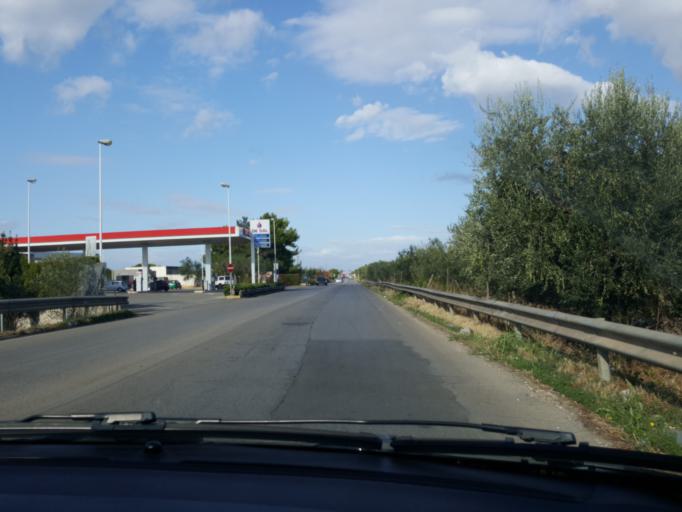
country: IT
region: Apulia
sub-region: Provincia di Bari
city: Triggiano
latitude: 41.0565
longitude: 16.9290
